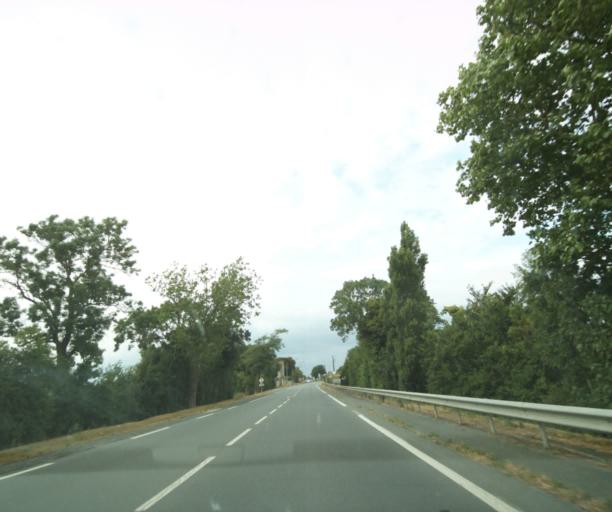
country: FR
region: Poitou-Charentes
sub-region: Departement de la Charente-Maritime
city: Marans
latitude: 46.2939
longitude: -0.9917
